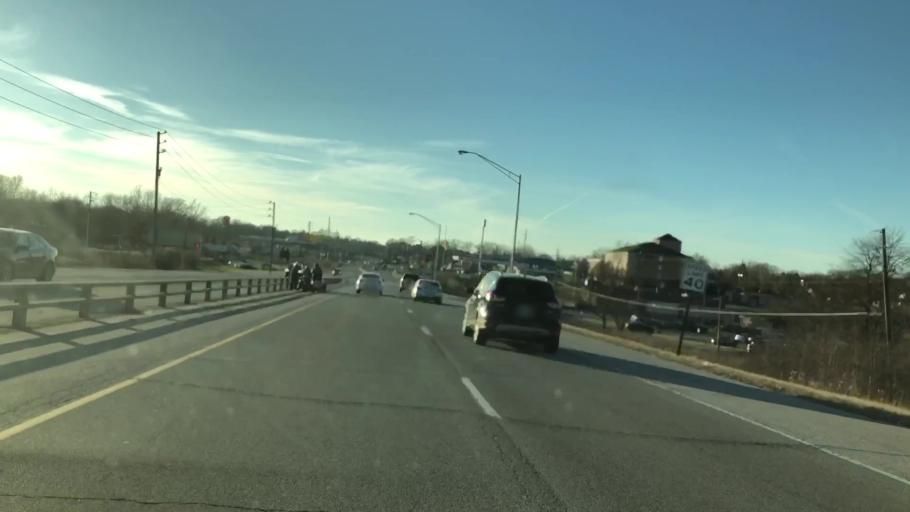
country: US
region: Indiana
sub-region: Marion County
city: Southport
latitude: 39.6657
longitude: -86.0924
